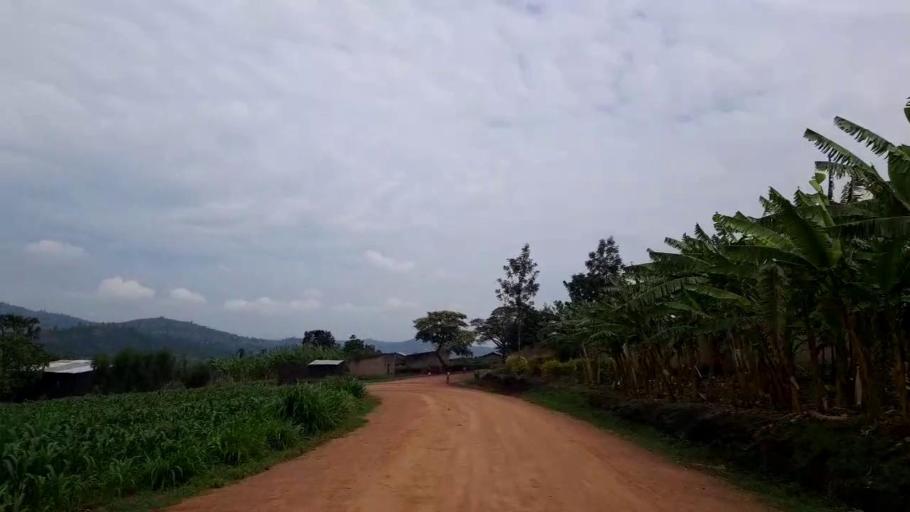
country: RW
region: Northern Province
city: Byumba
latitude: -1.4993
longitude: 30.2325
